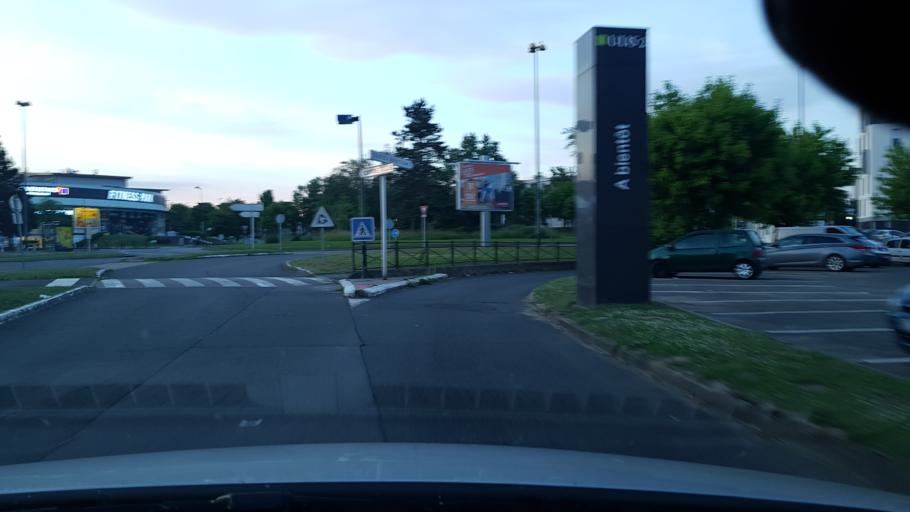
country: FR
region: Ile-de-France
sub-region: Departement de l'Essonne
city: Les Ulis
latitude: 48.6761
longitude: 2.1746
